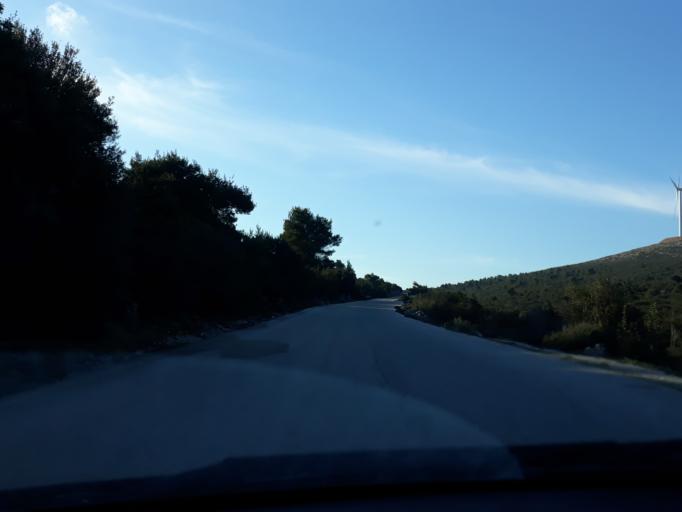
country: GR
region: Attica
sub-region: Nomarchia Dytikis Attikis
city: Fyli
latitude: 38.1601
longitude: 23.6235
